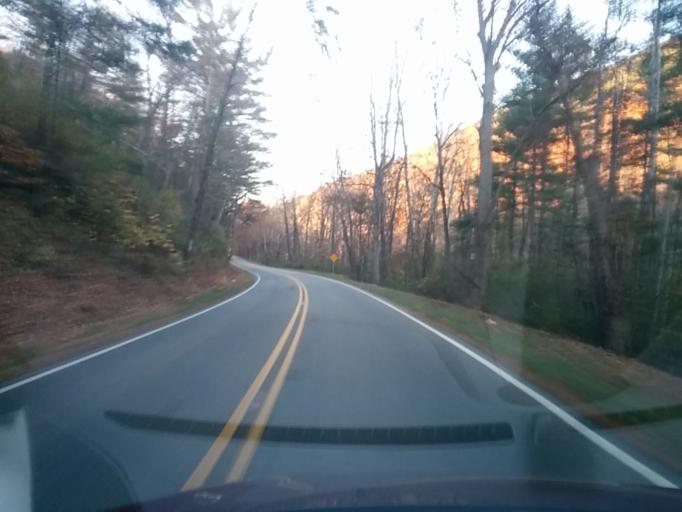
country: US
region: Virginia
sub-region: Rockbridge County
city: East Lexington
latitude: 37.9641
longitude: -79.4845
